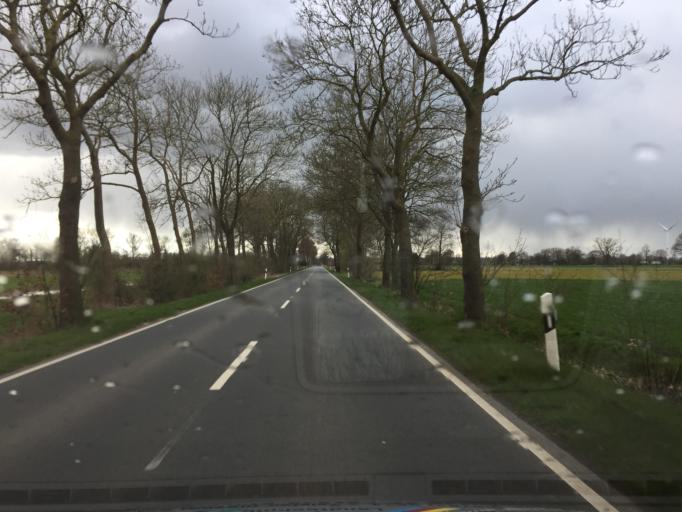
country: DE
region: Lower Saxony
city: Riede
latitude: 52.9518
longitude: 8.9355
